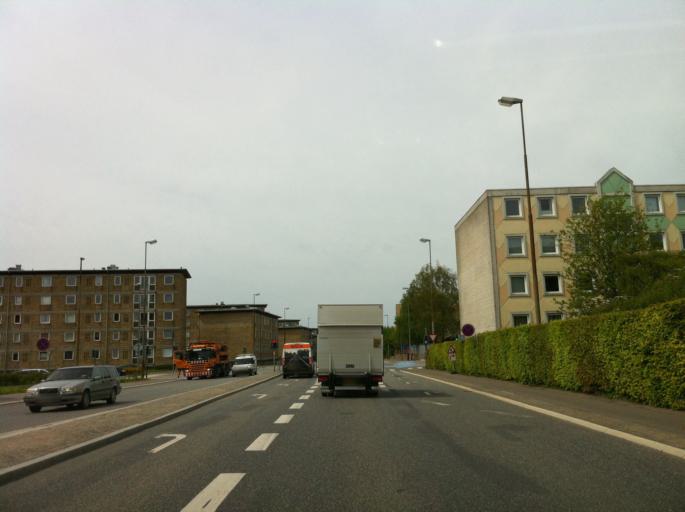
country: DK
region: Zealand
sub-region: Roskilde Kommune
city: Roskilde
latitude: 55.6307
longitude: 12.0938
